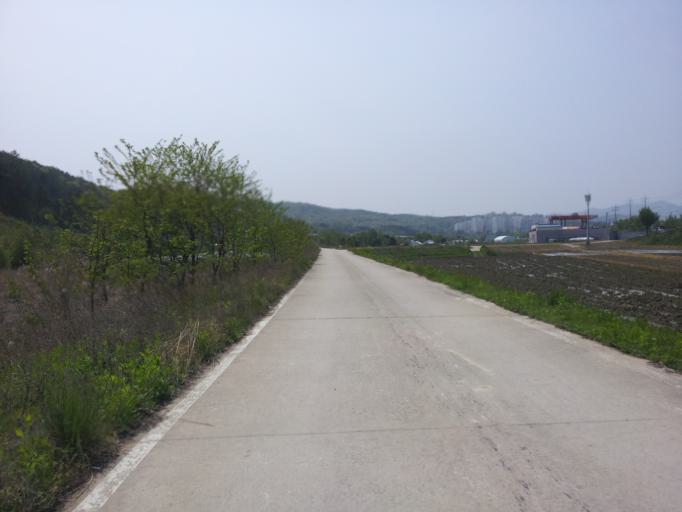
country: KR
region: Daejeon
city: Daejeon
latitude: 36.2660
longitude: 127.2874
